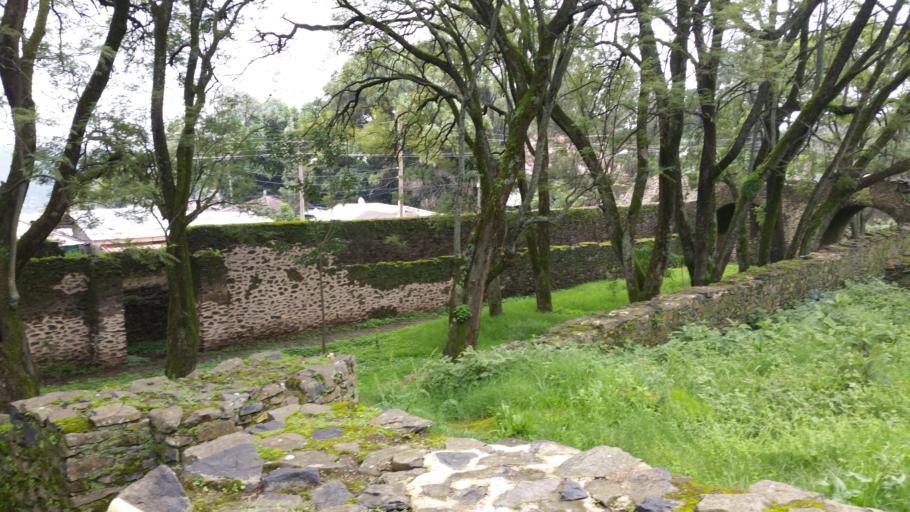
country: ET
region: Amhara
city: Gondar
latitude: 12.6078
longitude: 37.4703
